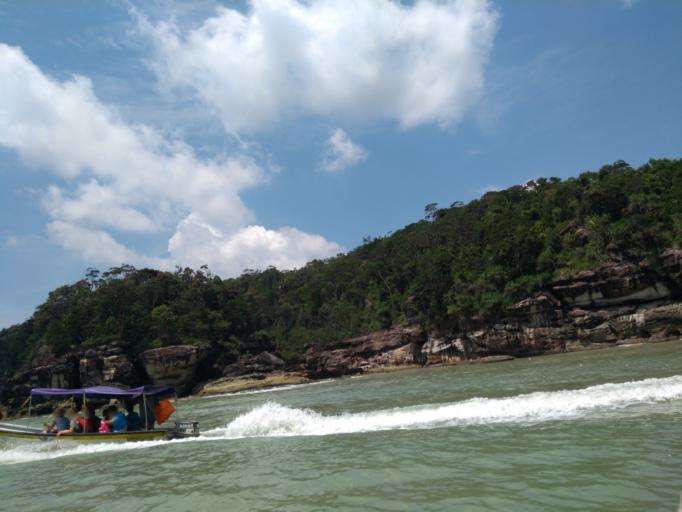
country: MY
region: Sarawak
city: Kuching
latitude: 1.7310
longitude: 110.4444
